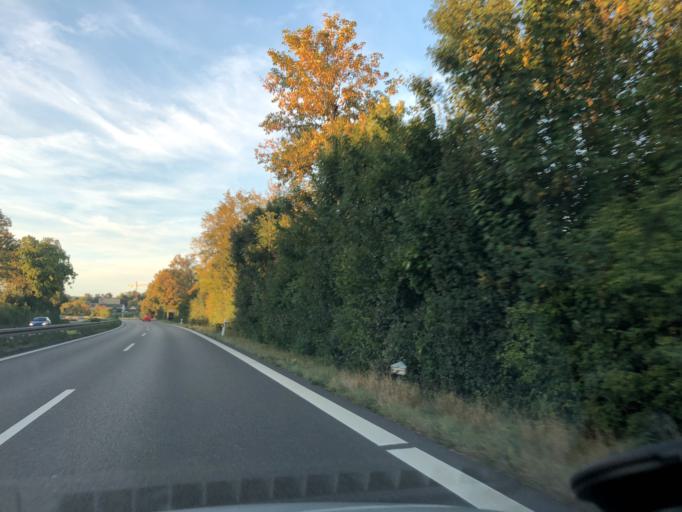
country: DE
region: Baden-Wuerttemberg
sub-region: Regierungsbezirk Stuttgart
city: Kornwestheim
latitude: 48.8752
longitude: 9.1970
